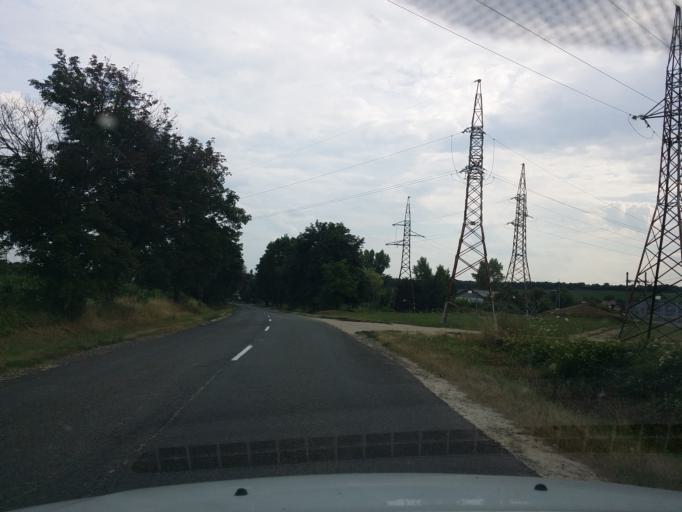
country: HU
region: Nograd
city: Bercel
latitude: 47.8903
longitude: 19.3689
